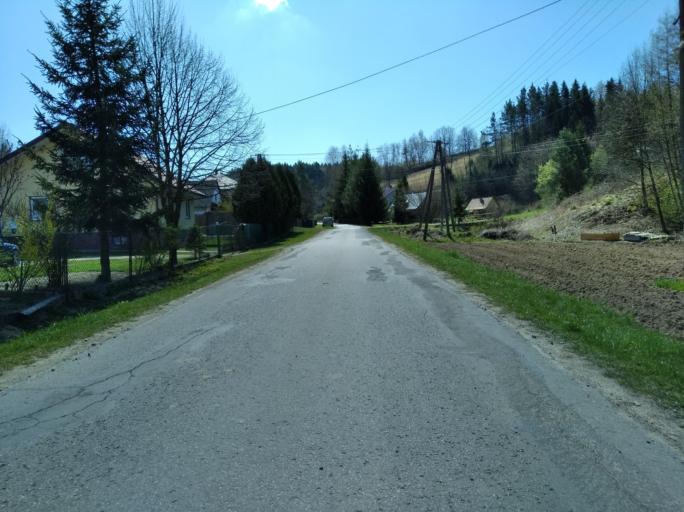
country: PL
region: Subcarpathian Voivodeship
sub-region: Powiat brzozowski
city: Dydnia
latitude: 49.7283
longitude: 22.1517
